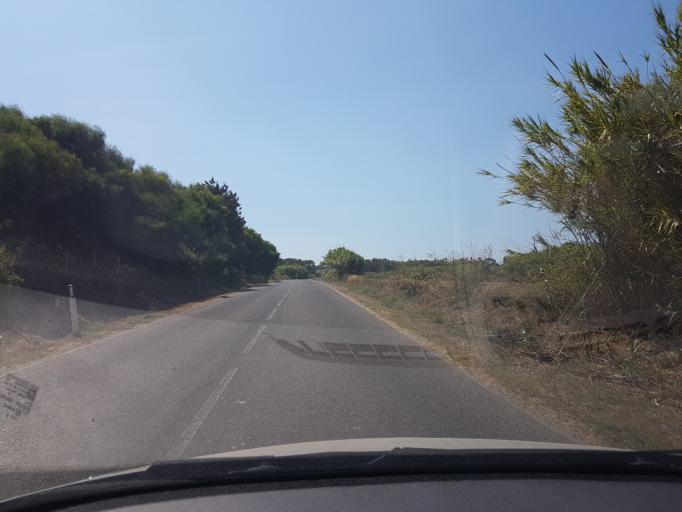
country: IT
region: Sardinia
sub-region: Provincia di Oristano
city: Riola Sardo
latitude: 40.0005
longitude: 8.5092
